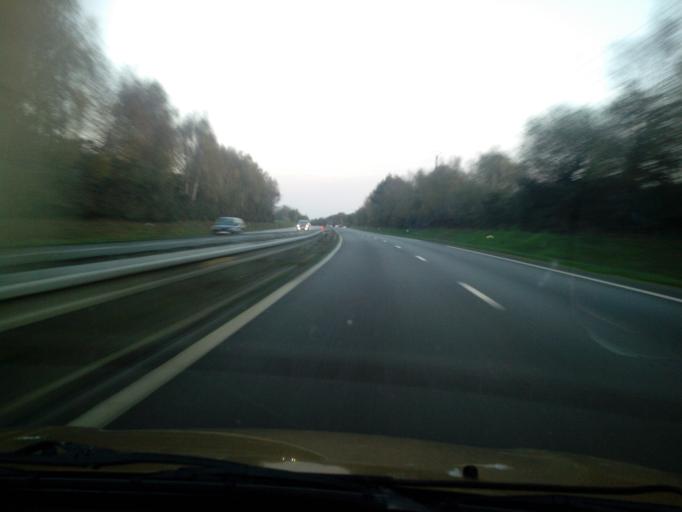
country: FR
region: Brittany
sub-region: Departement du Morbihan
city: Plumelin
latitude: 47.8908
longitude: -2.8803
